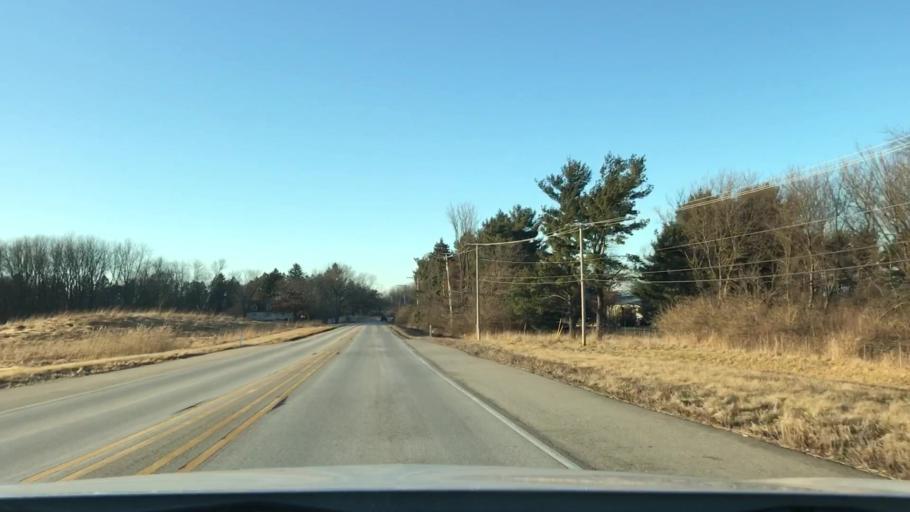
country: US
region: Illinois
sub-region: Kane County
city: Gilberts
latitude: 42.0886
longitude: -88.3947
